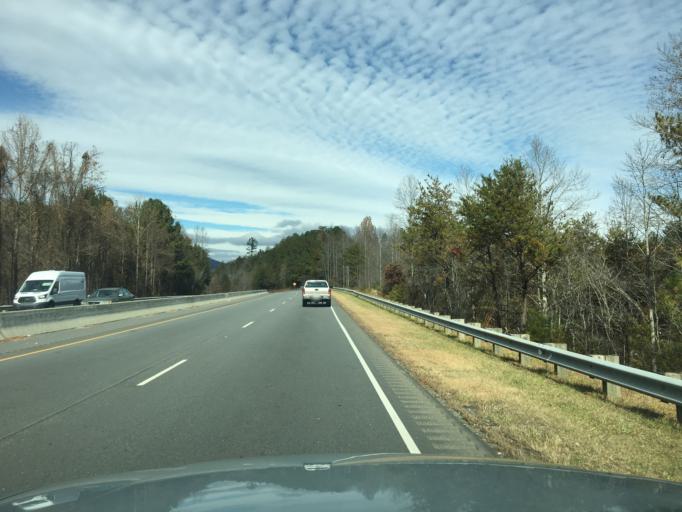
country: US
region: North Carolina
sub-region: McDowell County
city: Marion
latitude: 35.6939
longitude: -82.0299
